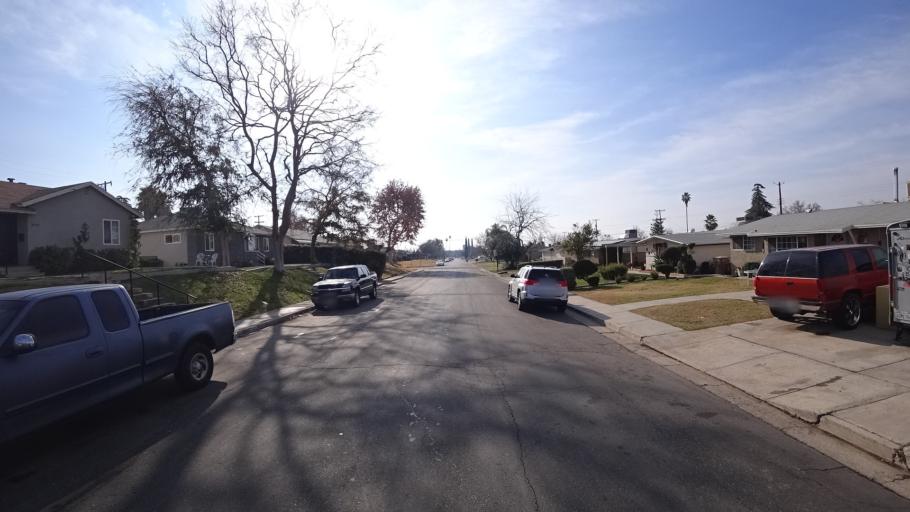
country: US
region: California
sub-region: Kern County
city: Oildale
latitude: 35.4008
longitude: -118.9734
